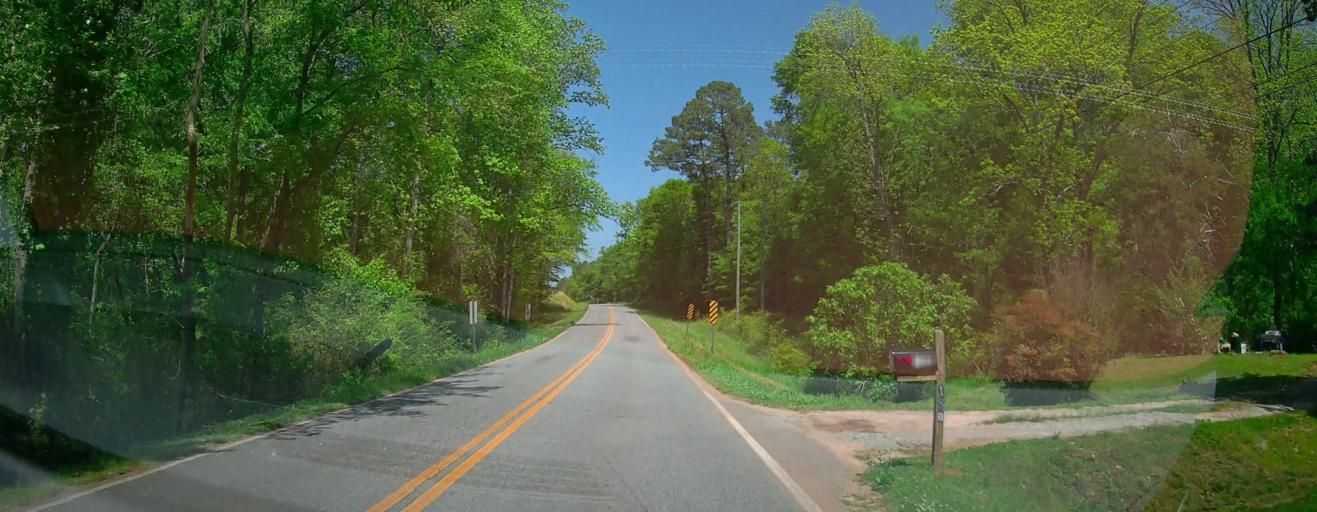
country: US
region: Georgia
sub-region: Jones County
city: Gray
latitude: 33.0008
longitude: -83.5614
